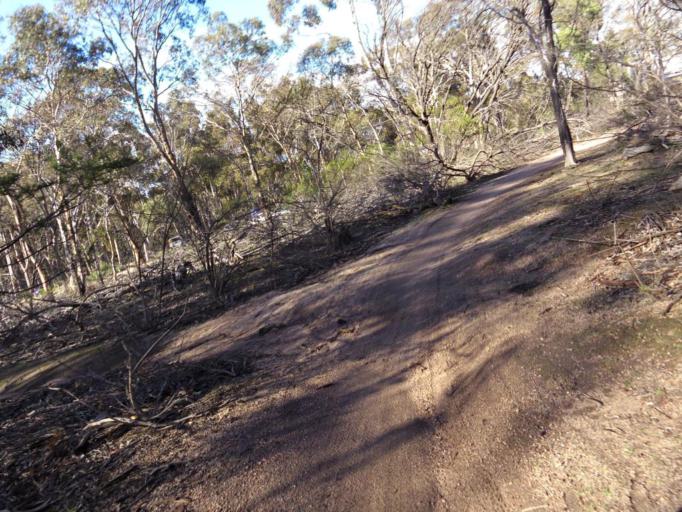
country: AU
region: Victoria
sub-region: Greater Geelong
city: Lara
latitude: -37.9622
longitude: 144.4098
